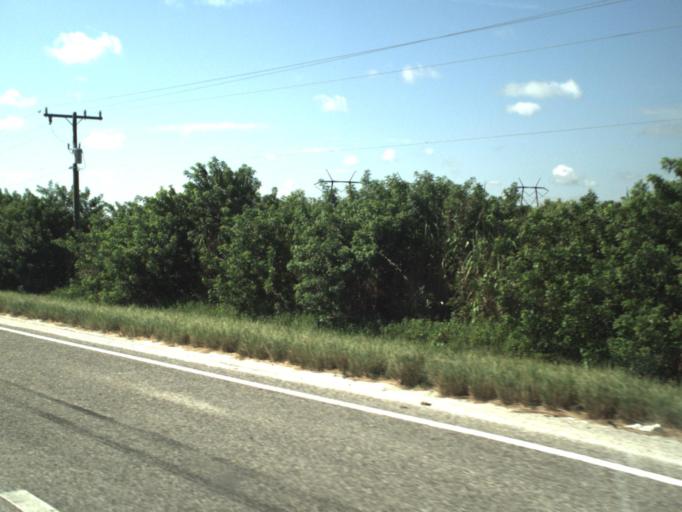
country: US
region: Florida
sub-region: Broward County
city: Weston
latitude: 26.3331
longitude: -80.5367
